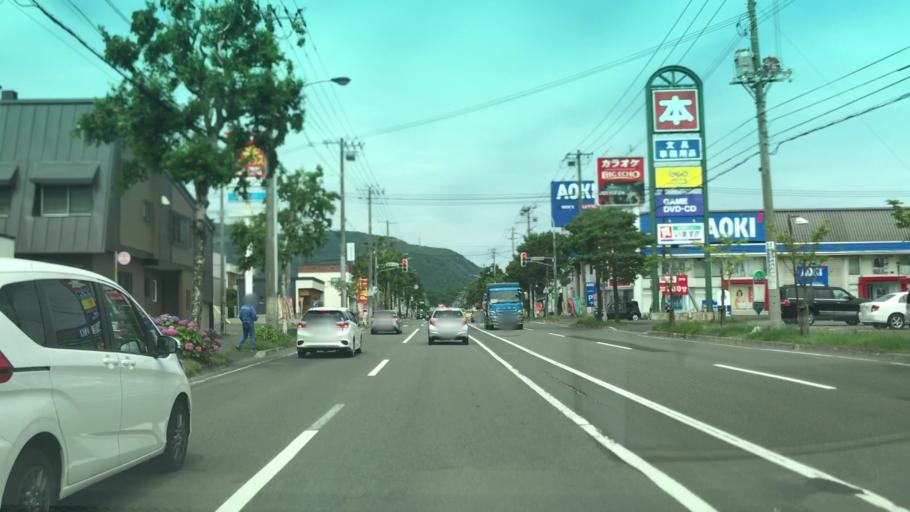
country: JP
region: Hokkaido
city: Sapporo
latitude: 43.0745
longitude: 141.2778
